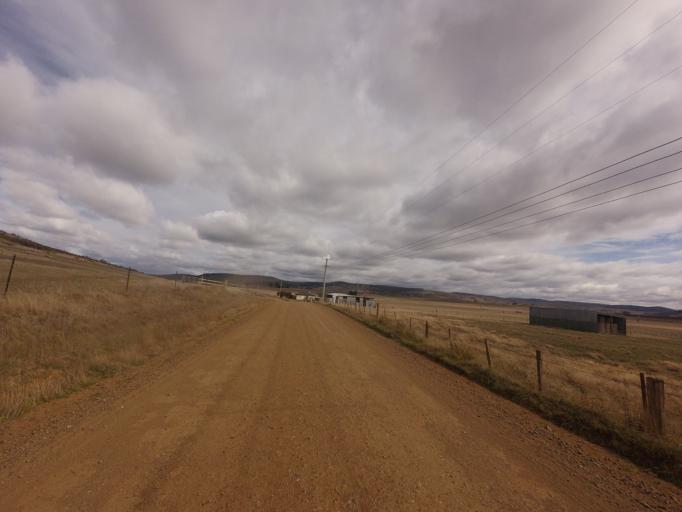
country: AU
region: Tasmania
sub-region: Brighton
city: Bridgewater
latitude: -42.4160
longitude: 147.3953
